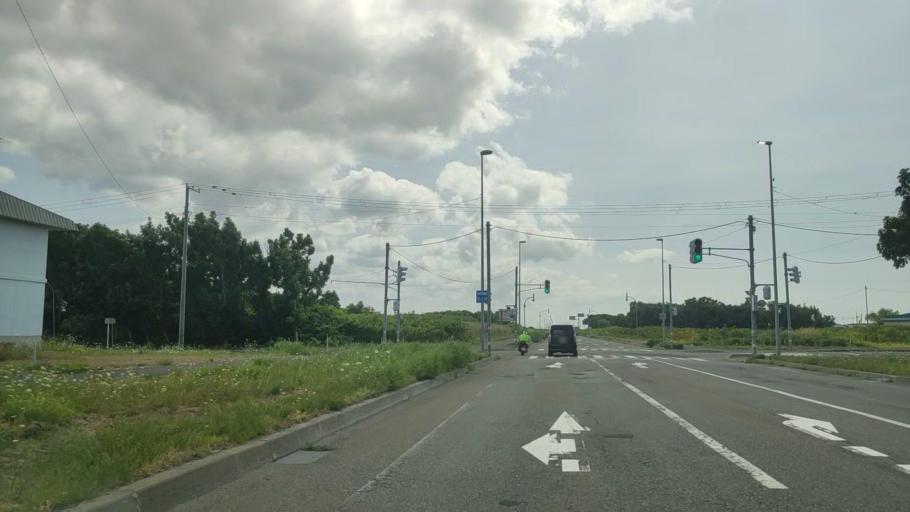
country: JP
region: Hokkaido
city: Makubetsu
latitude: 44.8779
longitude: 141.7504
